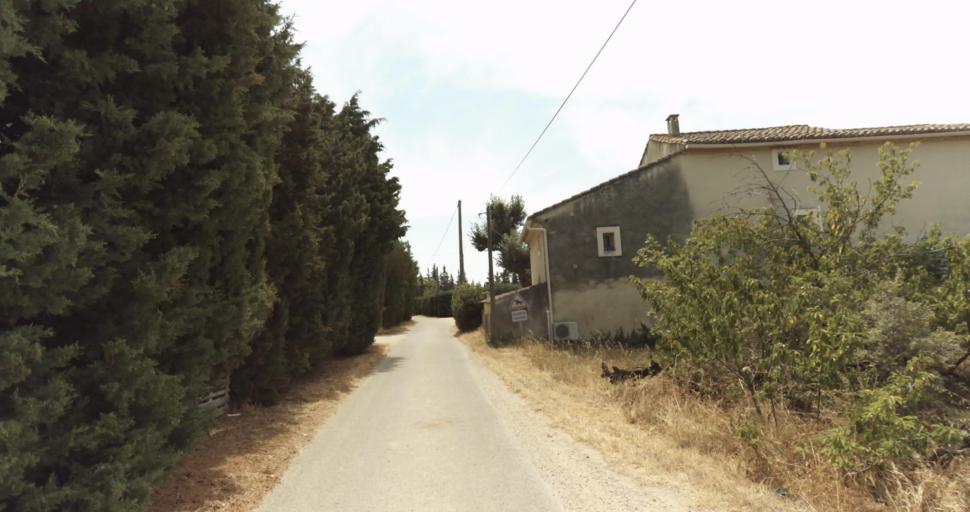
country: FR
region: Provence-Alpes-Cote d'Azur
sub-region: Departement du Vaucluse
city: Monteux
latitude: 44.0532
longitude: 4.9914
